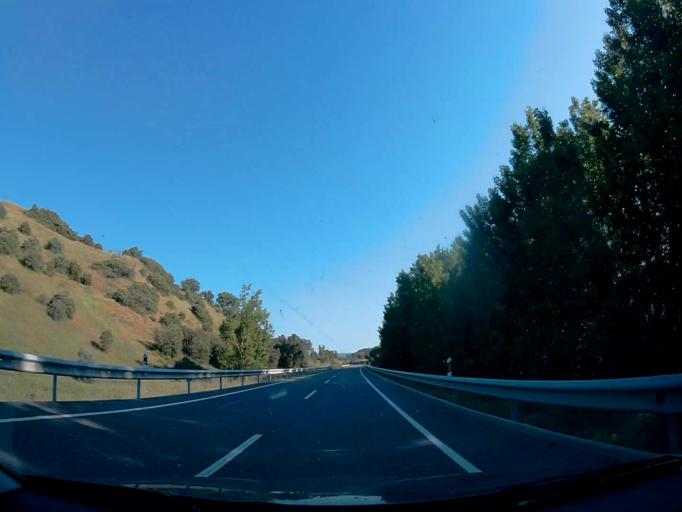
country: ES
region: Castille-La Mancha
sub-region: Province of Toledo
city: Escalona
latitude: 40.1759
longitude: -4.3996
